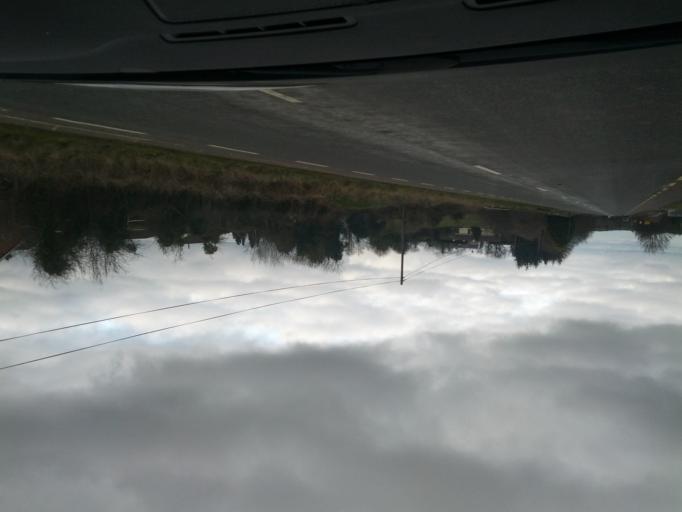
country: IE
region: Leinster
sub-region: An Iarmhi
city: Moate
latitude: 53.3971
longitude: -7.6533
